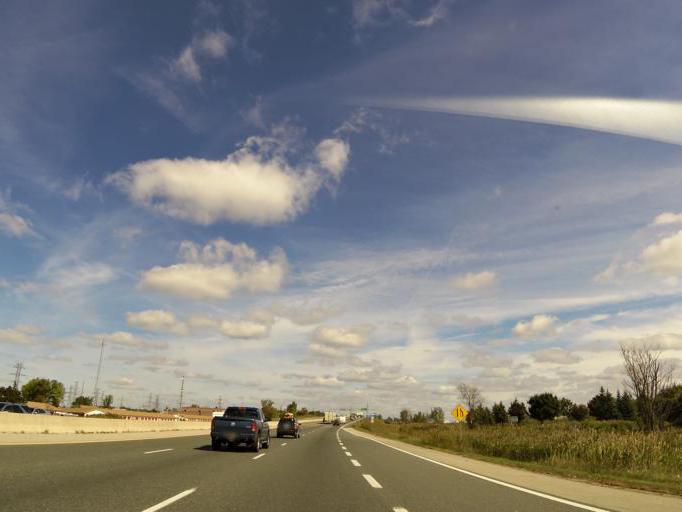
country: CA
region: Ontario
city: London
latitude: 42.9306
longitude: -81.2011
